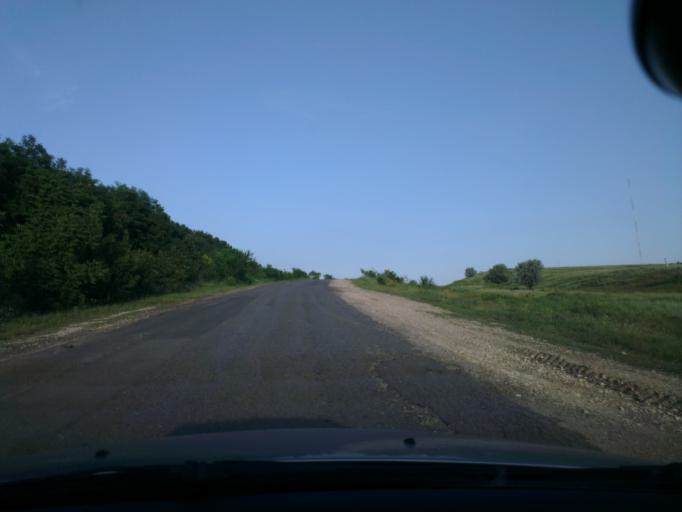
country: MD
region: Cantemir
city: Visniovca
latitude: 46.3653
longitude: 28.3911
